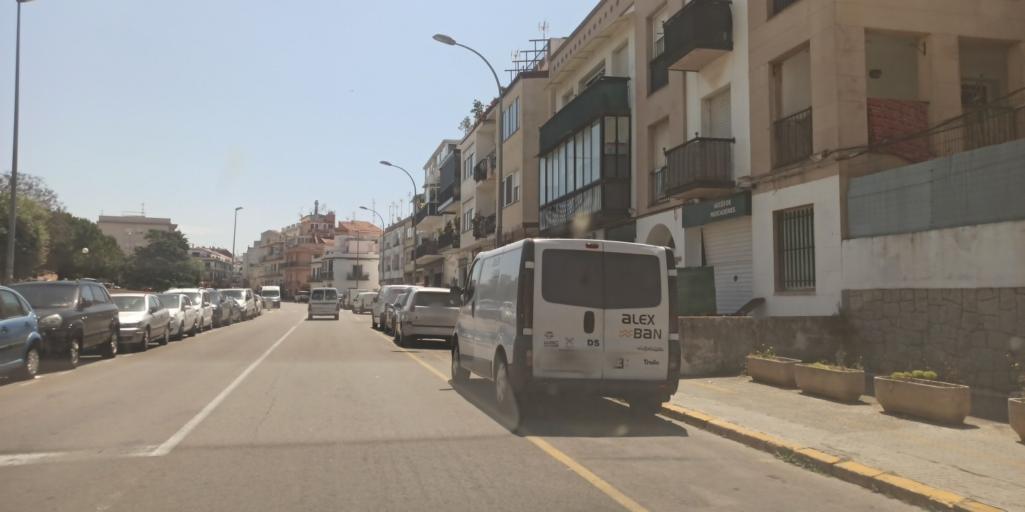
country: ES
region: Catalonia
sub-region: Provincia de Barcelona
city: Sitges
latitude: 41.2410
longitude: 1.8078
